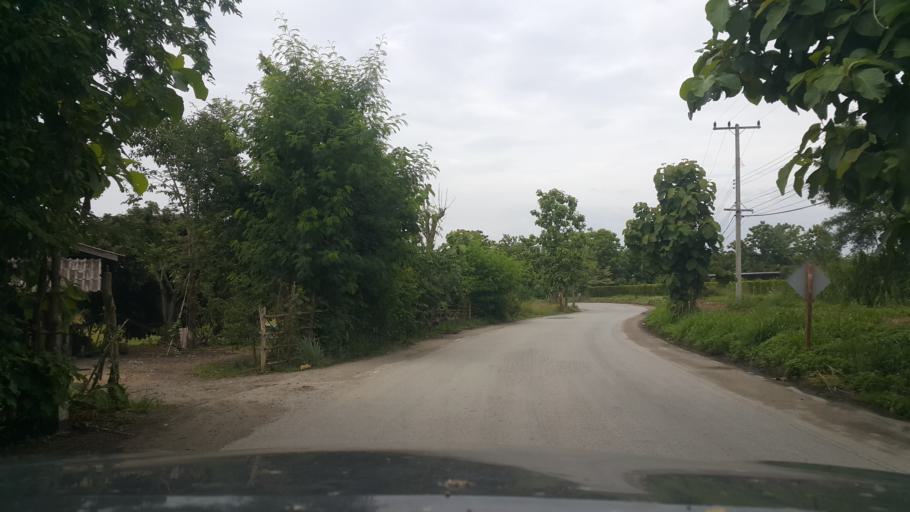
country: TH
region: Chiang Mai
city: San Pa Tong
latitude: 18.6644
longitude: 98.8356
